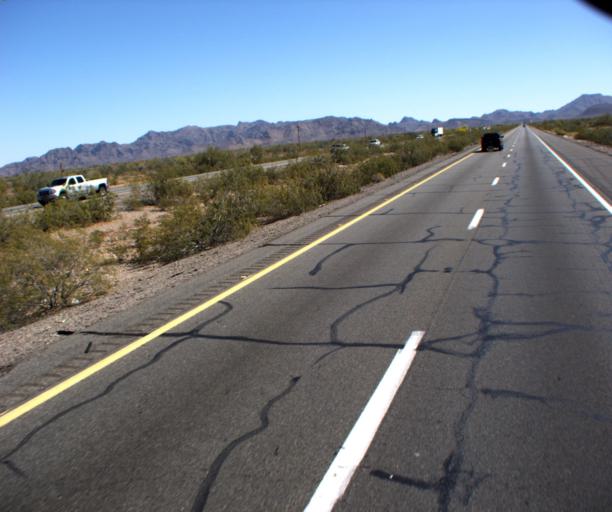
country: US
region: Arizona
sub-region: La Paz County
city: Quartzsite
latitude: 33.6720
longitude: -114.1482
